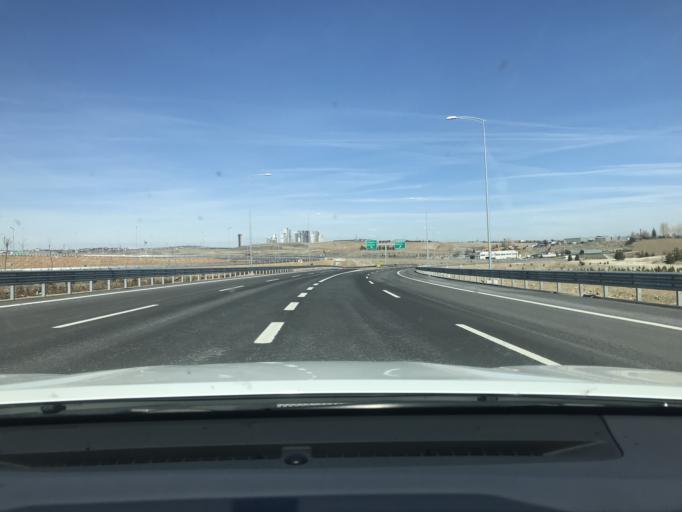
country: TR
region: Ankara
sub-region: Goelbasi
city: Golbasi
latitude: 39.7843
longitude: 32.7456
